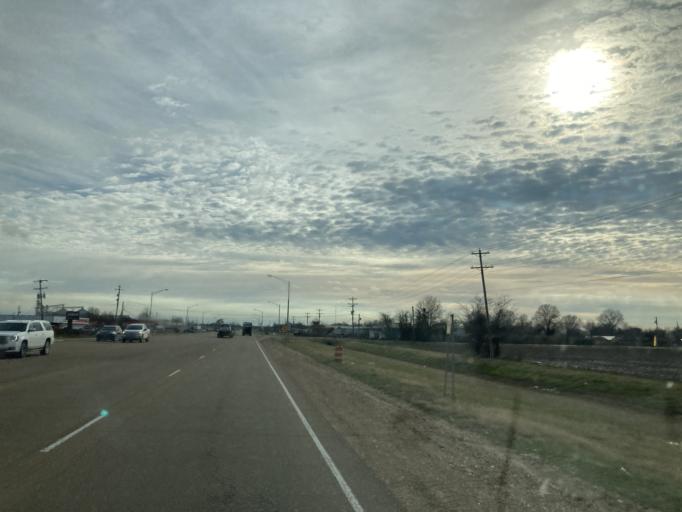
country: US
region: Mississippi
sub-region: Humphreys County
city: Belzoni
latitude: 33.1743
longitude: -90.4980
